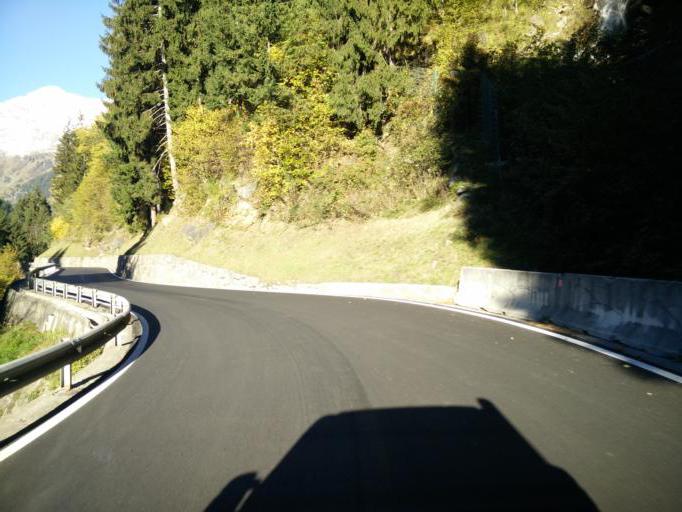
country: IT
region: Trentino-Alto Adige
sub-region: Bolzano
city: Moso in Passiria
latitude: 46.8248
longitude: 11.1924
